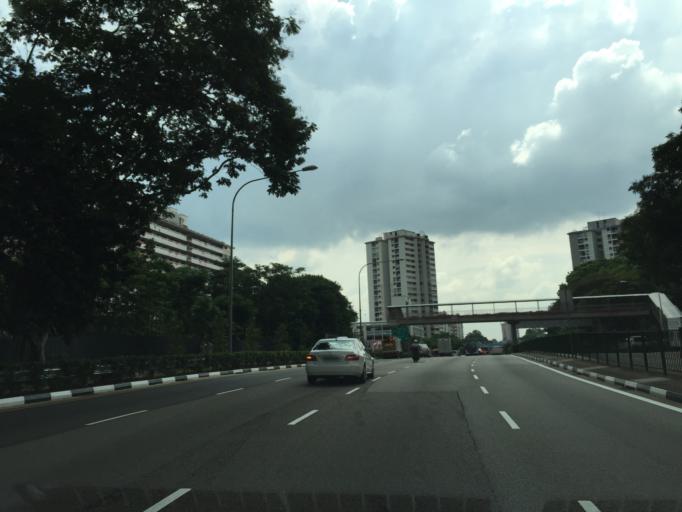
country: SG
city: Singapore
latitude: 1.3151
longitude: 103.8051
